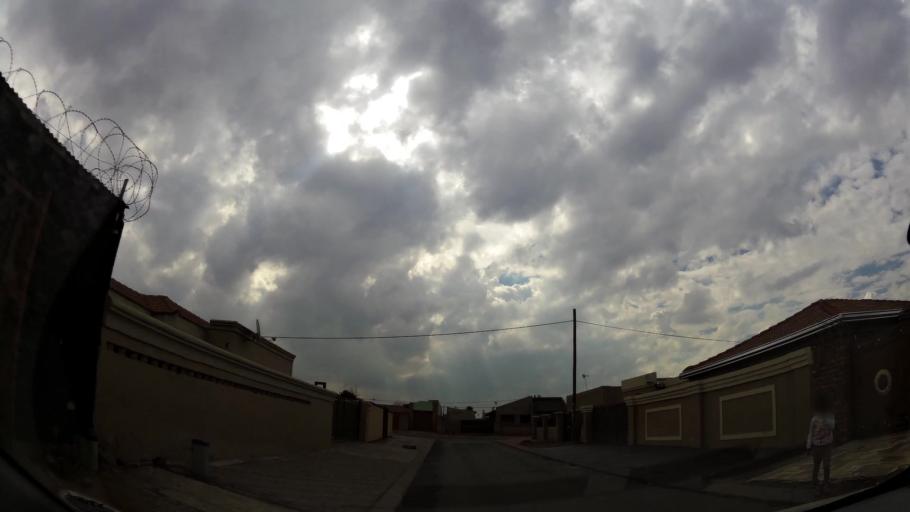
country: ZA
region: Gauteng
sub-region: Ekurhuleni Metropolitan Municipality
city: Germiston
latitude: -26.3845
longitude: 28.1606
